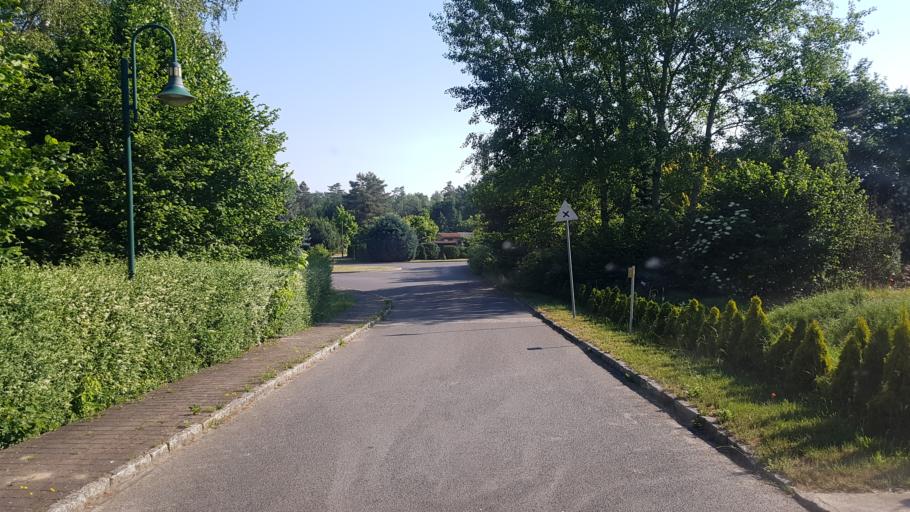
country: DE
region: Brandenburg
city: Lebusa
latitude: 51.7821
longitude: 13.3967
